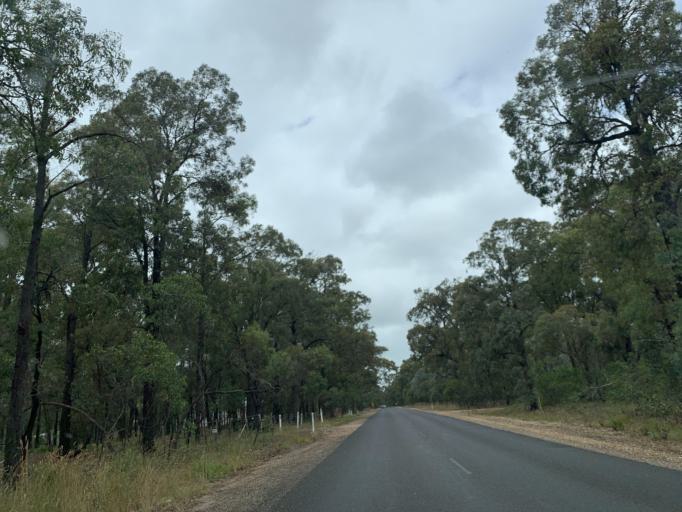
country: AU
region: Victoria
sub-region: Wellington
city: Heyfield
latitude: -37.9353
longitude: 146.7963
